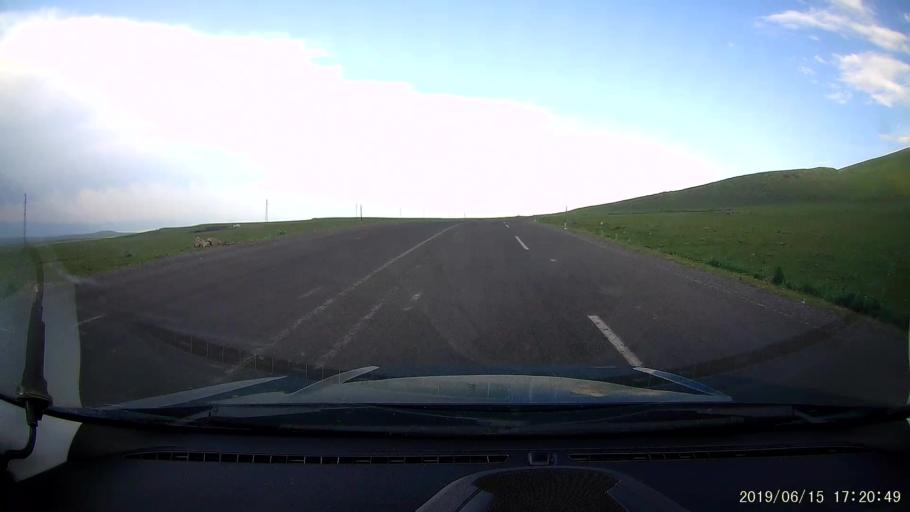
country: TR
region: Kars
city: Basgedikler
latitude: 40.6169
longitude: 43.3112
